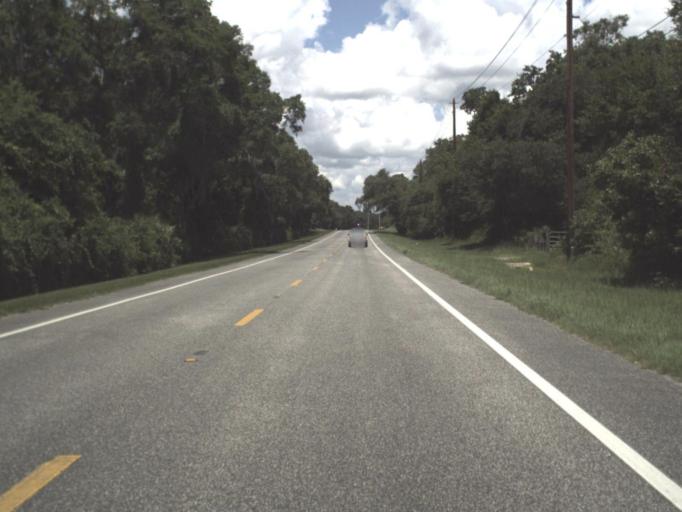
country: US
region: Florida
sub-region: Putnam County
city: Crescent City
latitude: 29.4893
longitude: -81.5792
